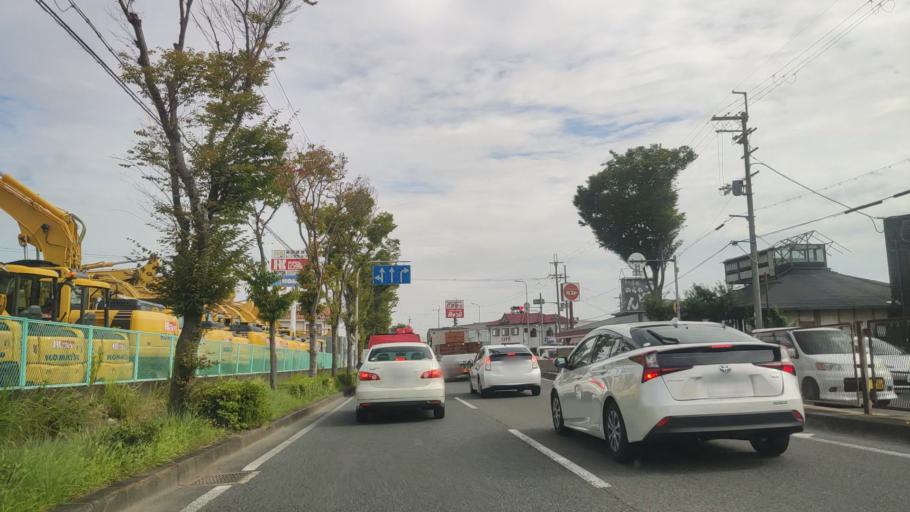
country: JP
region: Osaka
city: Tondabayashicho
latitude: 34.5131
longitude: 135.6038
